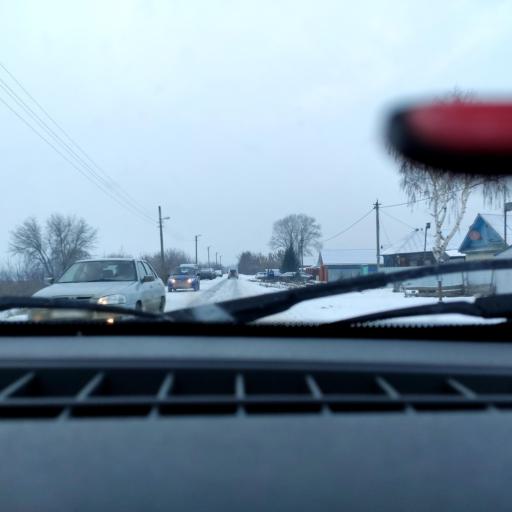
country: RU
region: Bashkortostan
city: Blagoveshchensk
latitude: 54.8984
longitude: 56.0208
